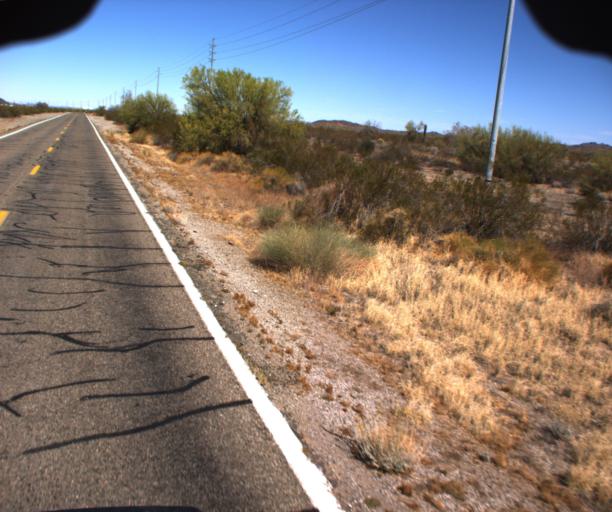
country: US
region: Arizona
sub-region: La Paz County
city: Salome
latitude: 33.7382
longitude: -113.7360
